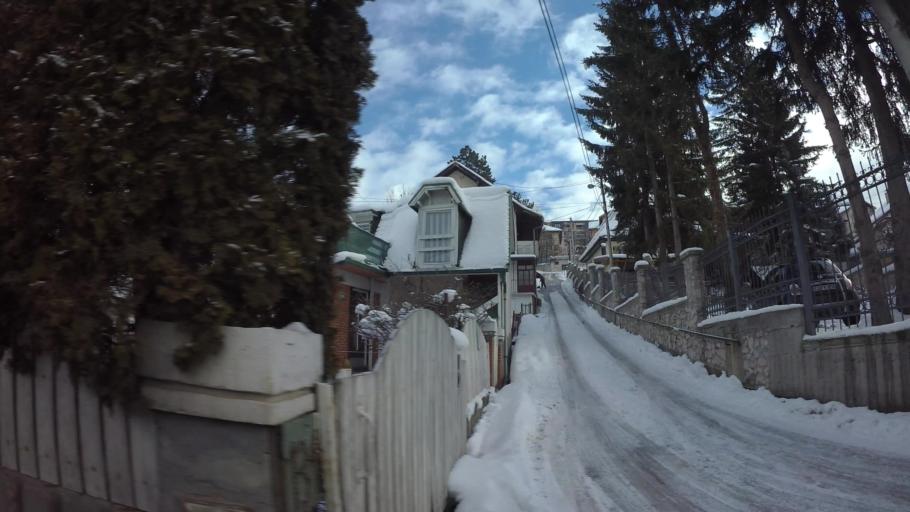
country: BA
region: Federation of Bosnia and Herzegovina
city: Kobilja Glava
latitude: 43.8785
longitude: 18.4139
